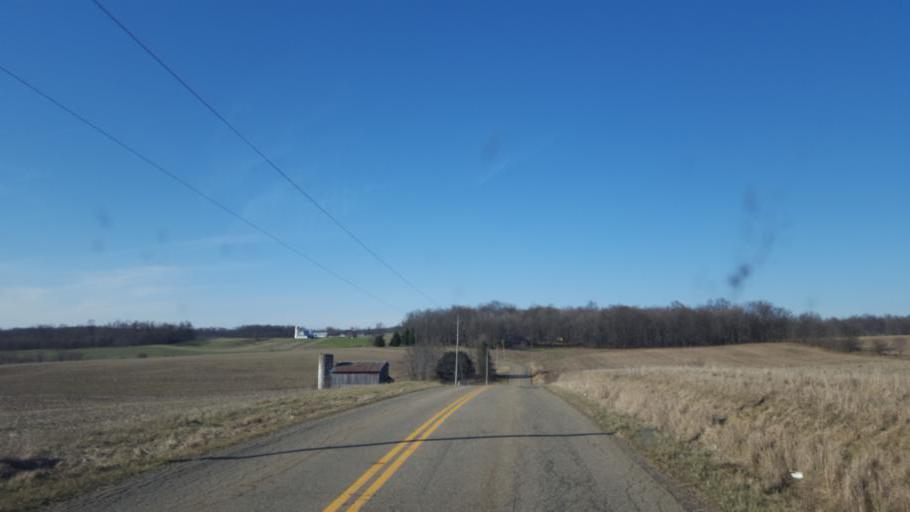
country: US
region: Ohio
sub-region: Knox County
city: Gambier
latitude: 40.4780
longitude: -82.3806
